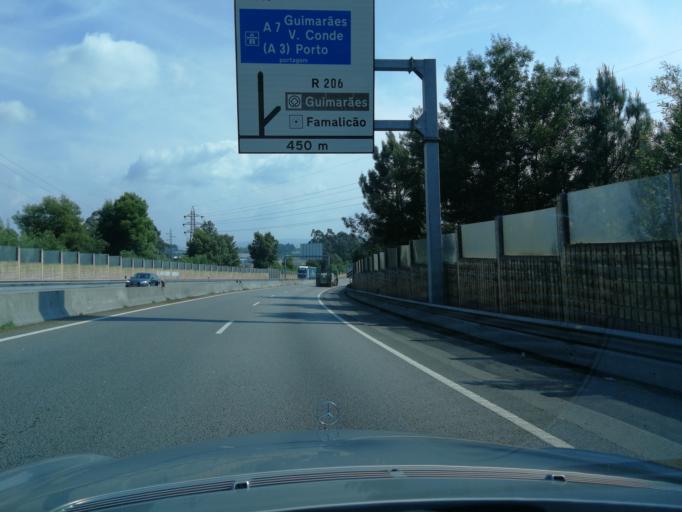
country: PT
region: Braga
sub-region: Vila Nova de Famalicao
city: Vila Nova de Famalicao
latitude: 41.4215
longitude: -8.5116
